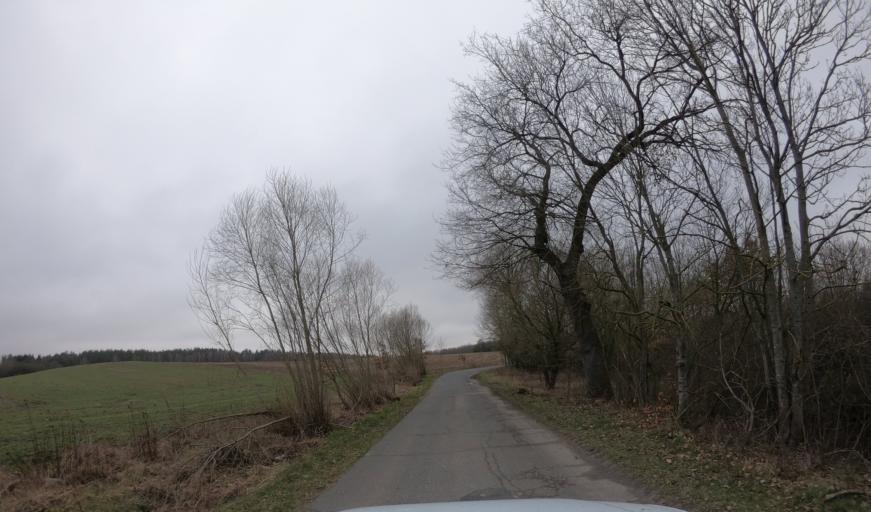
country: PL
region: West Pomeranian Voivodeship
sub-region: Powiat gryficki
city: Ploty
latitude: 53.8469
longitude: 15.2759
